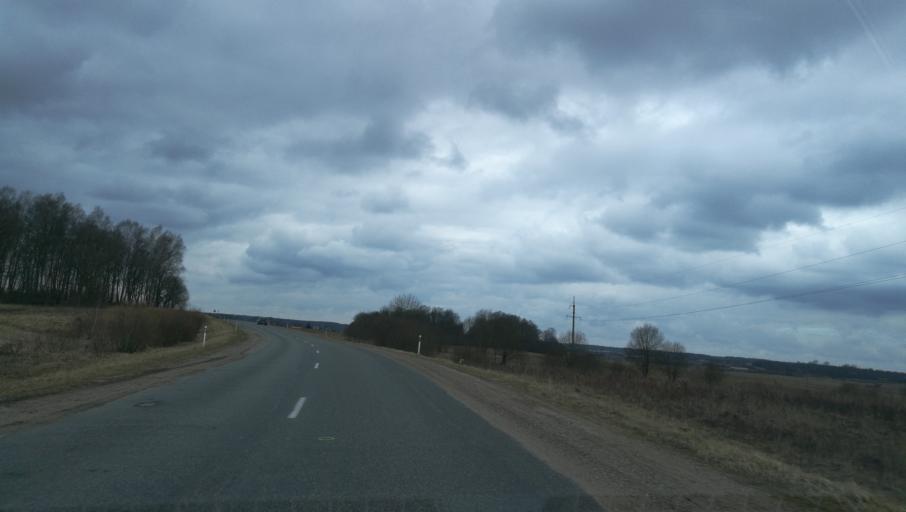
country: LT
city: Grigiskes
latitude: 54.8662
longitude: 25.0337
